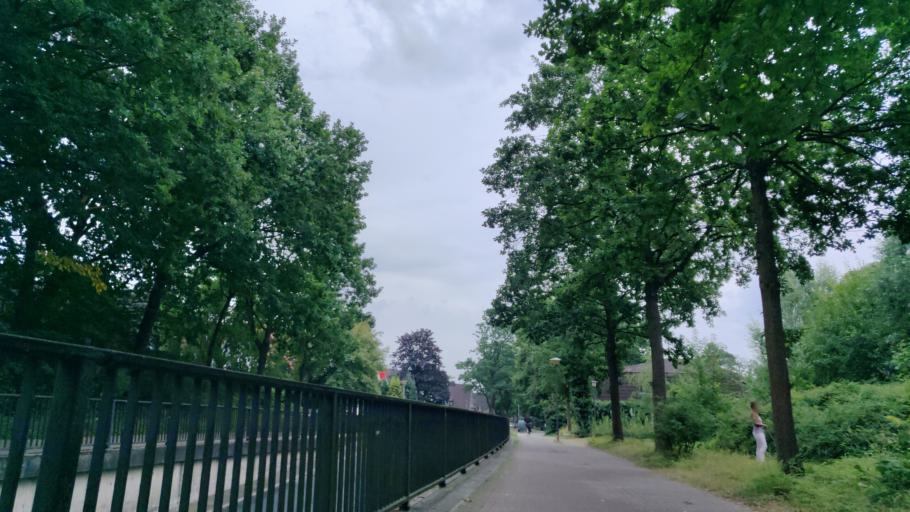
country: DE
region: Lower Saxony
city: Lilienthal
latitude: 53.0947
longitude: 8.8971
